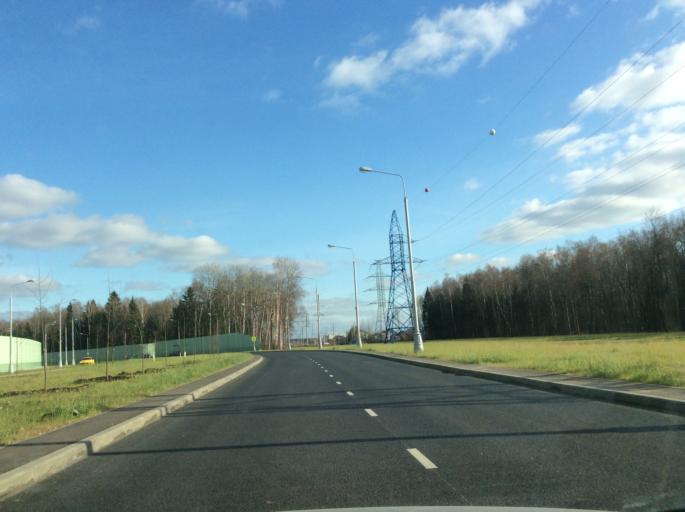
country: RU
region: Moskovskaya
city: Vatutinki
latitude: 55.4821
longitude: 37.3681
